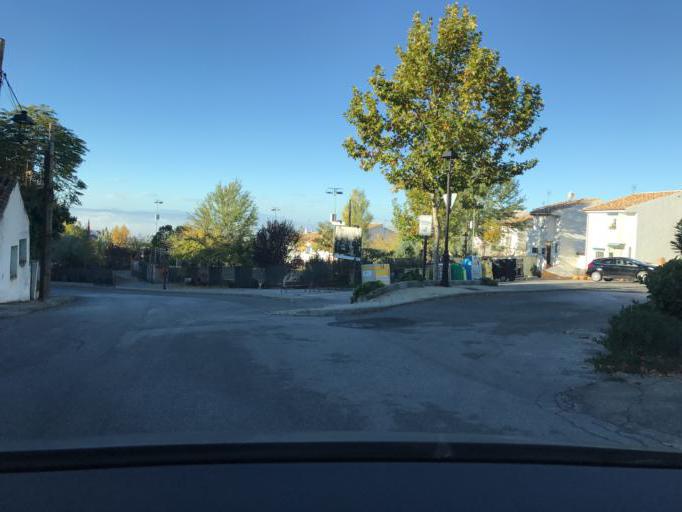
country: ES
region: Andalusia
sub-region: Provincia de Granada
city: Viznar
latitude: 37.2347
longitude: -3.5521
